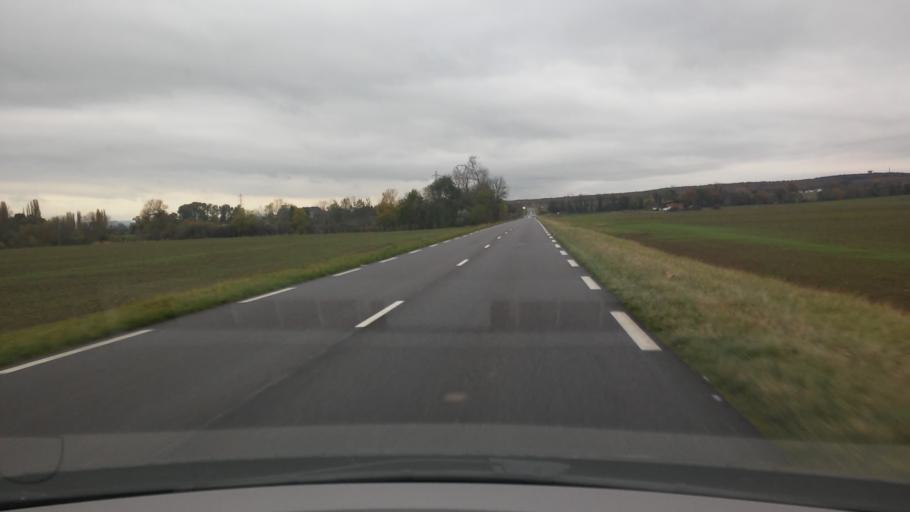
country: FR
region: Lorraine
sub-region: Departement de la Moselle
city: Bousse
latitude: 49.2606
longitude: 6.2012
